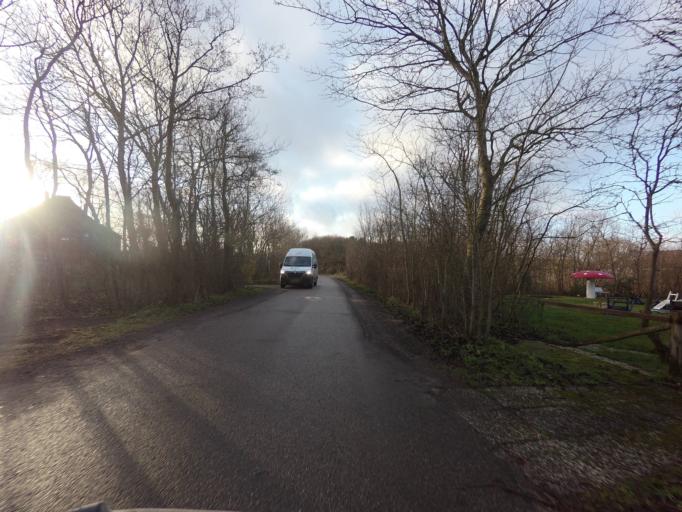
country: NL
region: North Holland
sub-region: Gemeente Texel
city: Den Burg
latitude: 53.0983
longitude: 4.7738
